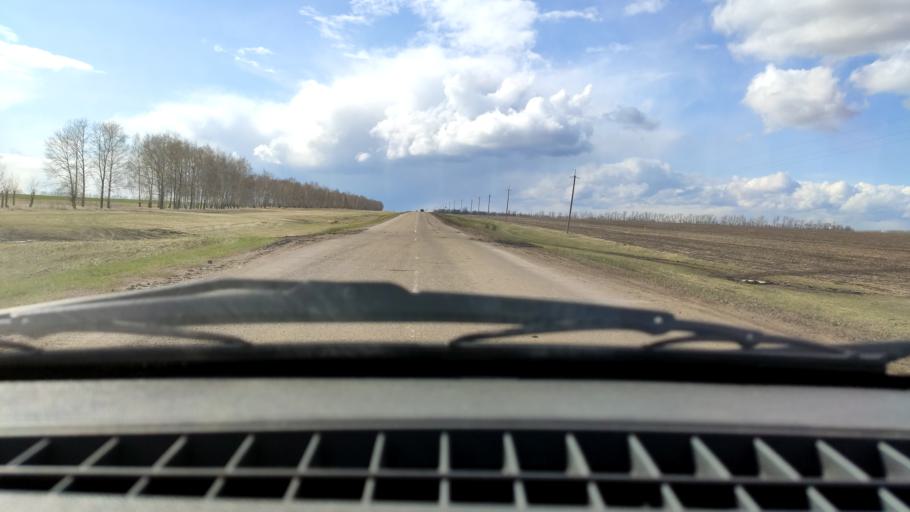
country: RU
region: Bashkortostan
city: Kushnarenkovo
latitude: 55.0989
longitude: 55.0467
